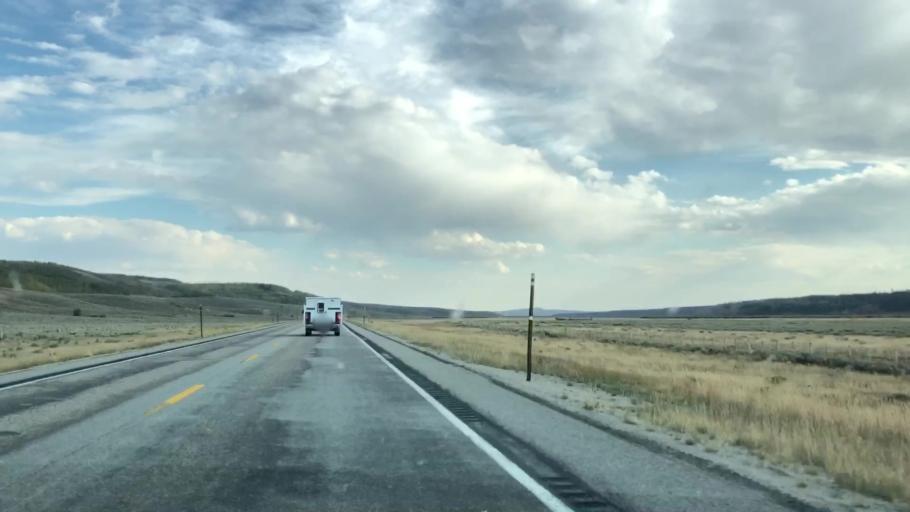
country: US
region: Wyoming
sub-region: Sublette County
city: Pinedale
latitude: 43.1045
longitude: -110.1709
